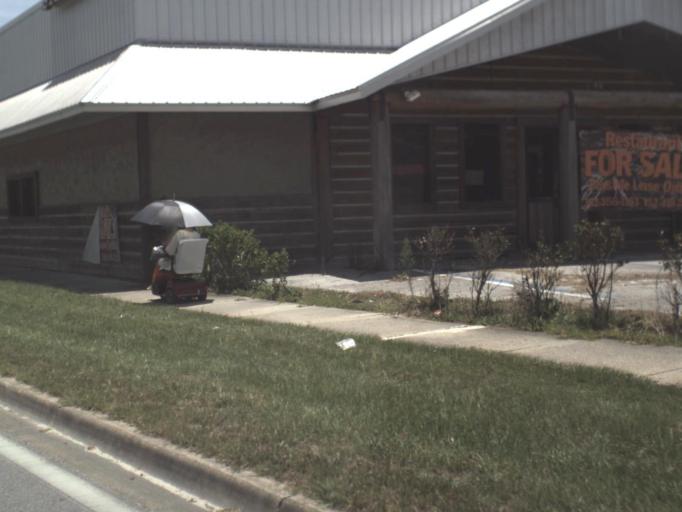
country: US
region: Florida
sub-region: Dixie County
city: Cross City
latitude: 29.6364
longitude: -83.1284
